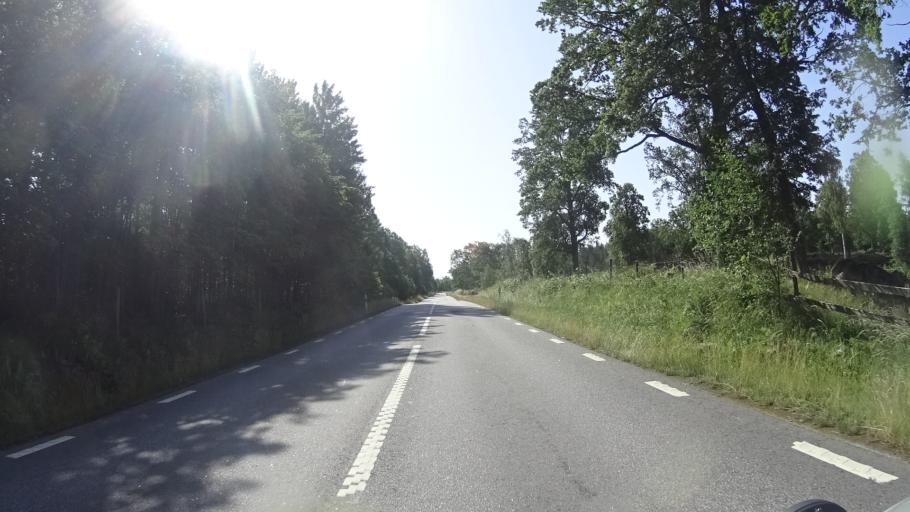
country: SE
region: OEstergoetland
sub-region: Atvidabergs Kommun
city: Atvidaberg
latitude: 58.0940
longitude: 16.1279
